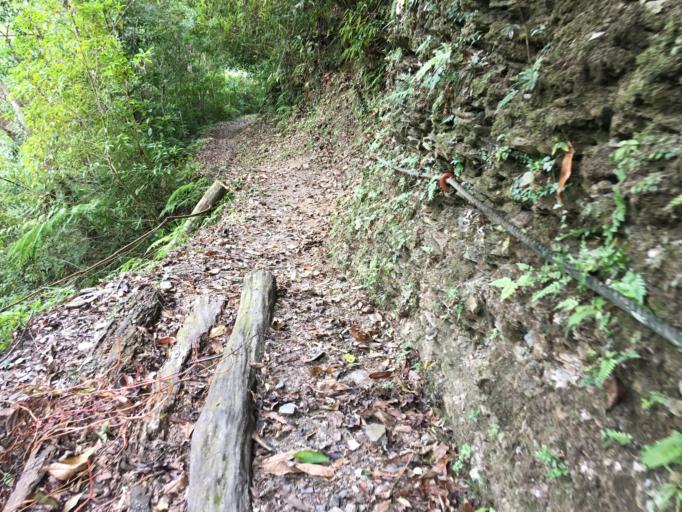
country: TW
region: Taiwan
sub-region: Yilan
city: Yilan
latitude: 24.4259
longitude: 121.7000
